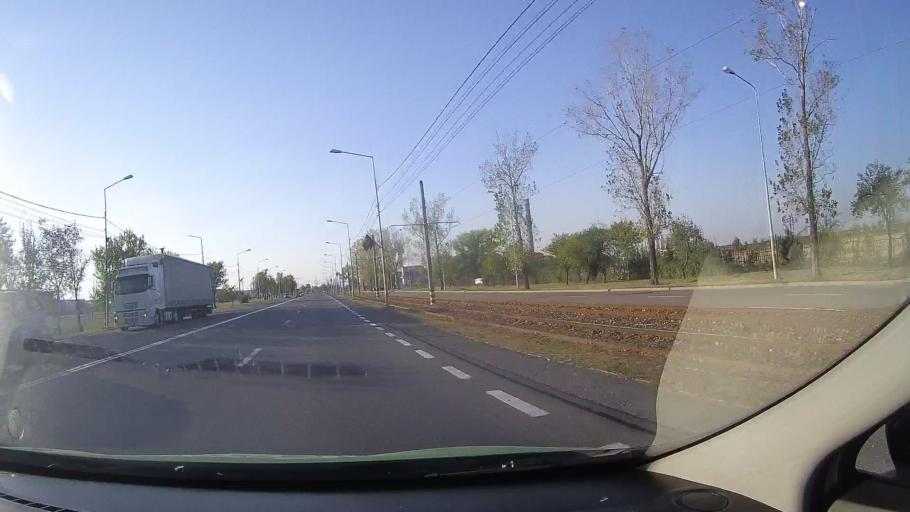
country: RO
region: Bihor
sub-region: Comuna Santandrei
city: Santandrei
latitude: 47.0833
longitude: 21.8872
